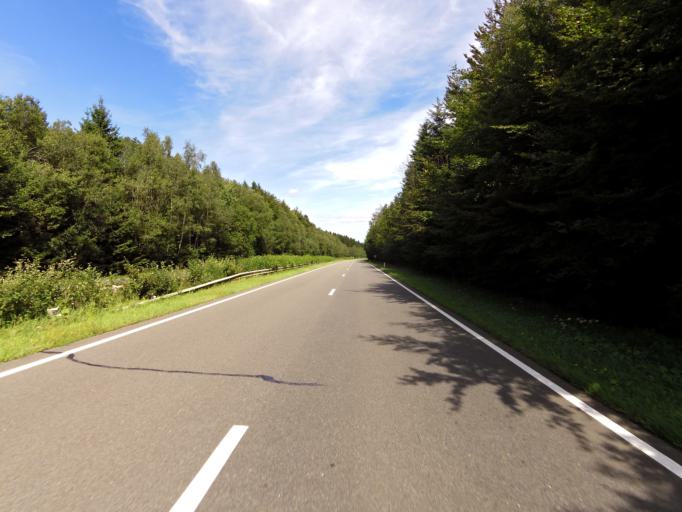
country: BE
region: Wallonia
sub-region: Province du Luxembourg
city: Tenneville
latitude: 50.0982
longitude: 5.4610
